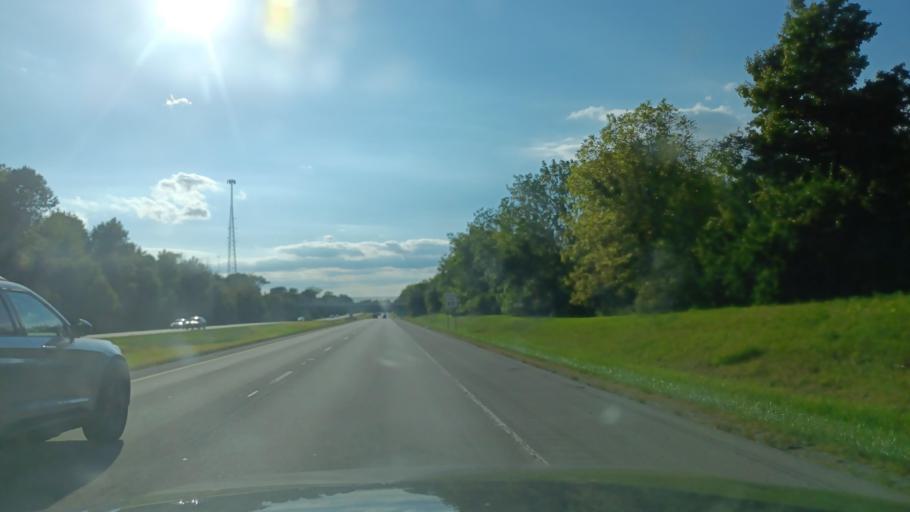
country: US
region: Ohio
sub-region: Greene County
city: Xenia
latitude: 39.6630
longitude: -83.9300
